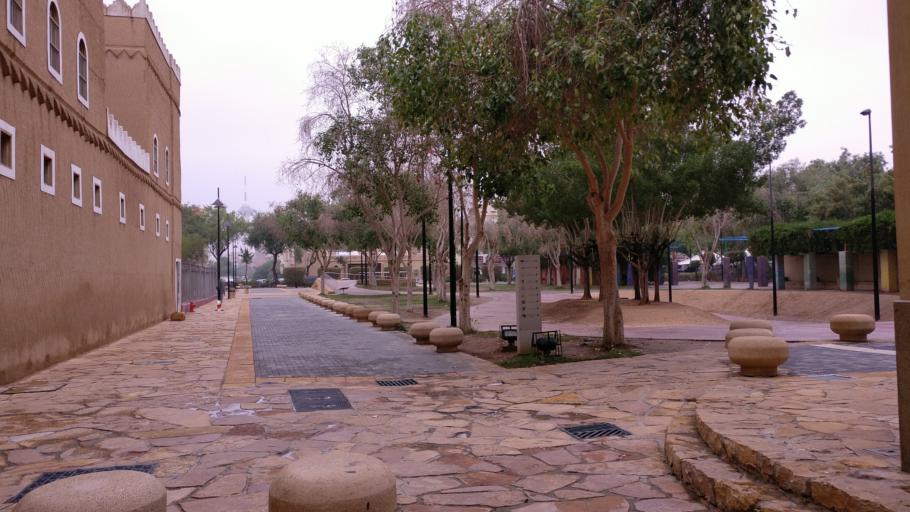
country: SA
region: Ar Riyad
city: Riyadh
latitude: 24.6470
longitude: 46.7084
